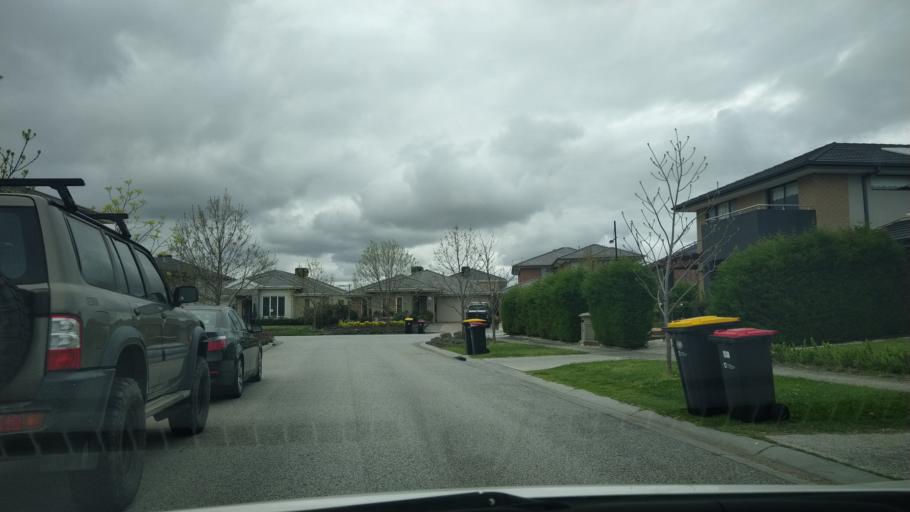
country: AU
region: Victoria
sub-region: Greater Dandenong
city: Keysborough
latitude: -38.0098
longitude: 145.1760
